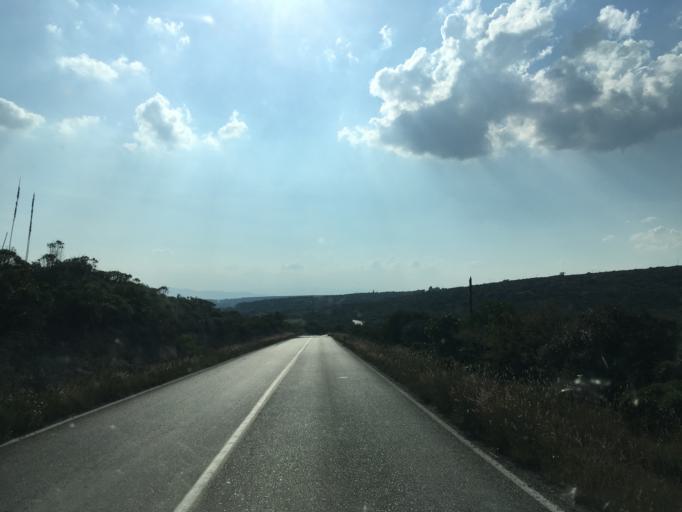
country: MX
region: Hidalgo
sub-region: Cardonal
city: Pozuelos
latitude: 20.6018
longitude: -99.1106
